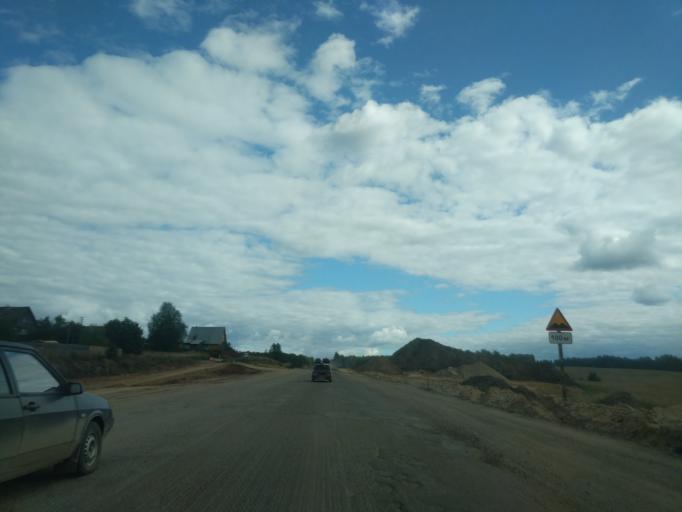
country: RU
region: Kostroma
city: Sudislavl'
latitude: 57.8745
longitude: 41.7354
